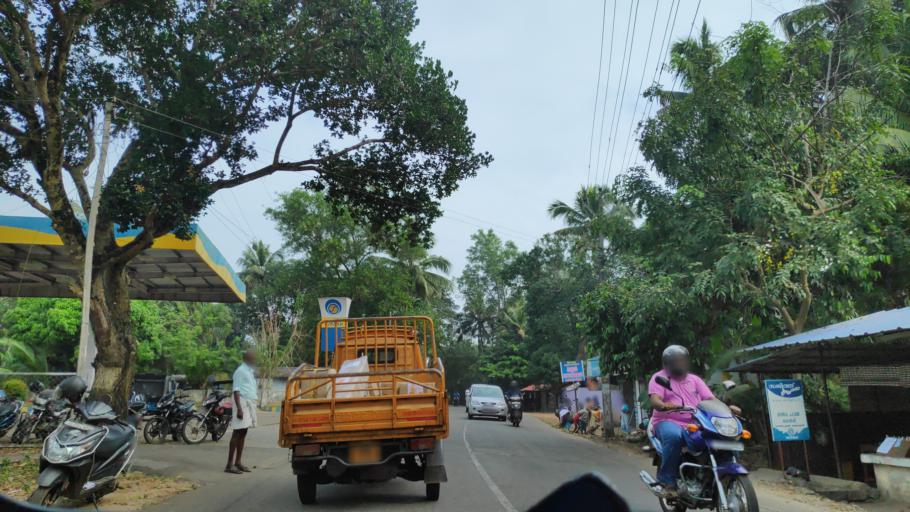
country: IN
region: Kerala
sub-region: Alappuzha
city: Vayalar
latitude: 9.7270
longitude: 76.3612
